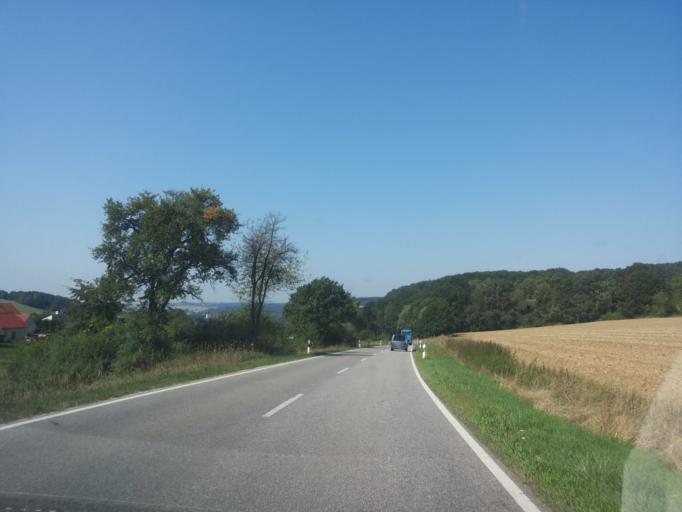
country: DE
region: Bavaria
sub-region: Lower Bavaria
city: Ihrlerstein
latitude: 48.8917
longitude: 11.8404
